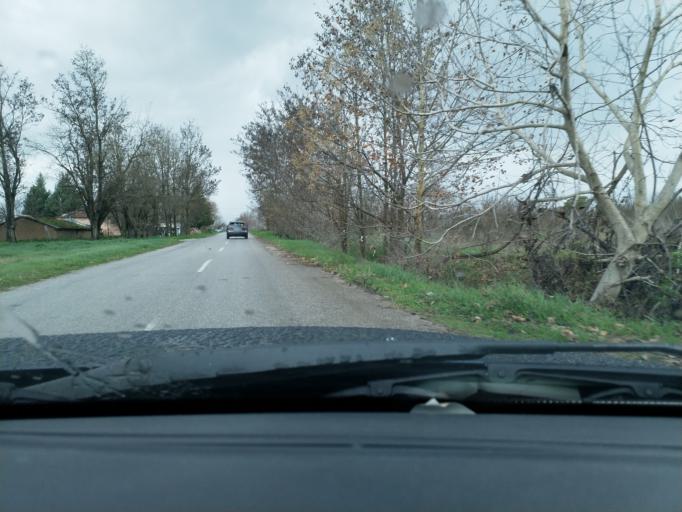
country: GR
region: Thessaly
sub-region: Trikala
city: Taxiarches
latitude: 39.5505
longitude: 21.8953
